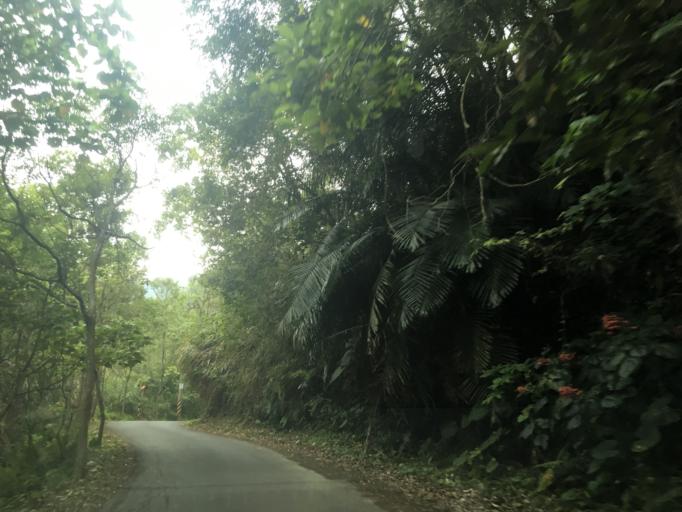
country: TW
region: Taiwan
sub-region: Taichung City
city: Taichung
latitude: 24.0568
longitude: 120.7750
